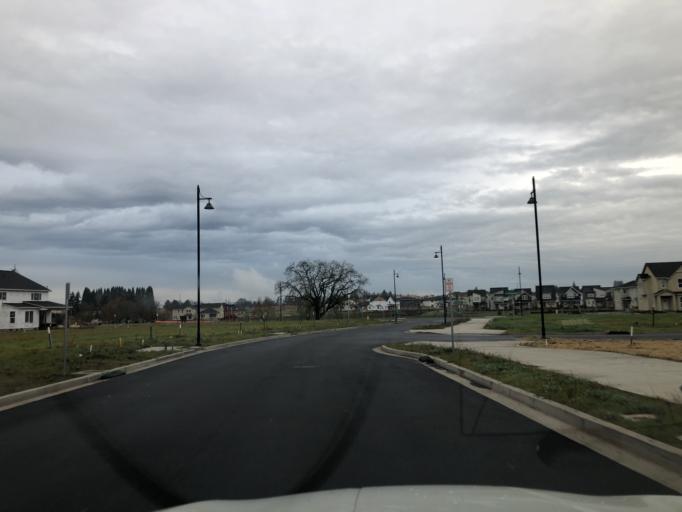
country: US
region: Oregon
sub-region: Washington County
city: Aloha
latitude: 45.4914
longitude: -122.9106
